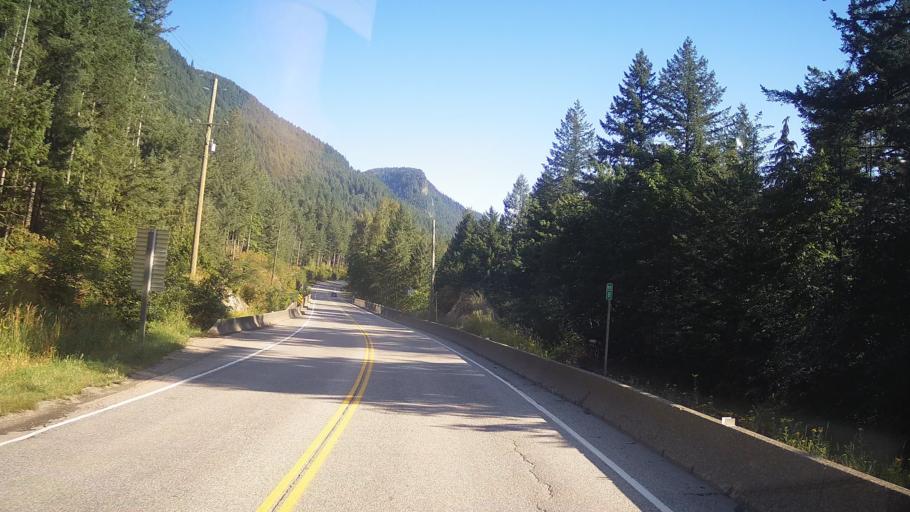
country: CA
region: British Columbia
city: Hope
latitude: 49.4295
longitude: -121.4378
